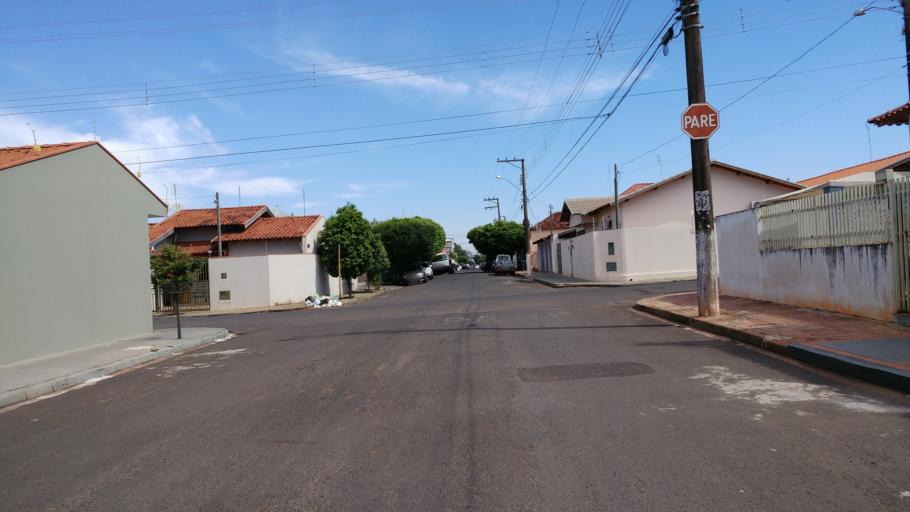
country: BR
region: Sao Paulo
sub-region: Paraguacu Paulista
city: Paraguacu Paulista
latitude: -22.4110
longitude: -50.5755
